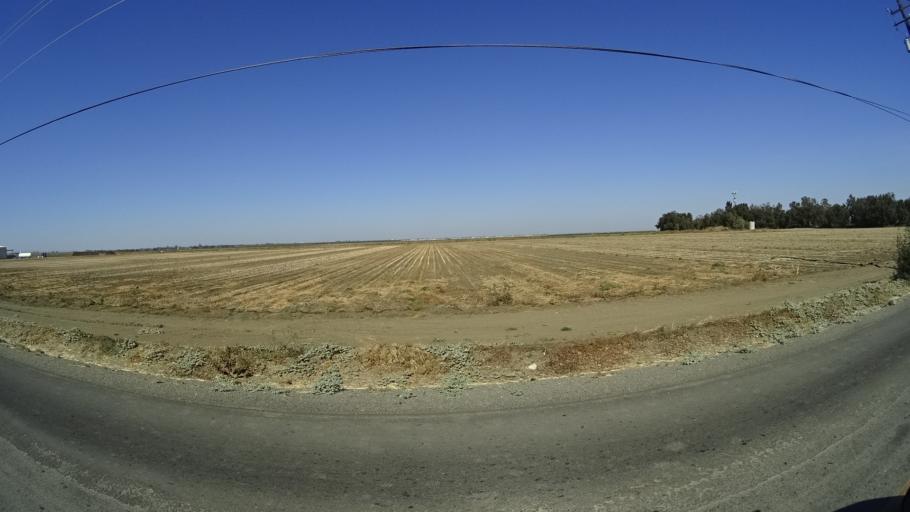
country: US
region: California
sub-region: Yolo County
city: Woodland
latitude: 38.6189
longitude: -121.7458
